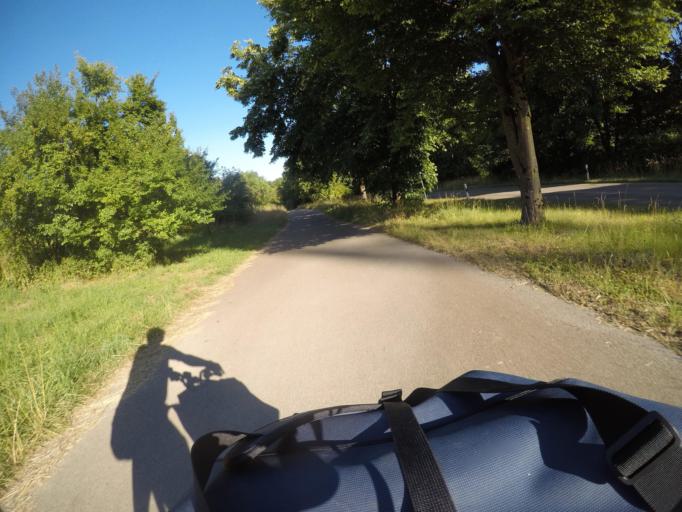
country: DE
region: Baden-Wuerttemberg
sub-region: Regierungsbezirk Stuttgart
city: Stuttgart Muehlhausen
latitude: 48.8657
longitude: 9.2423
